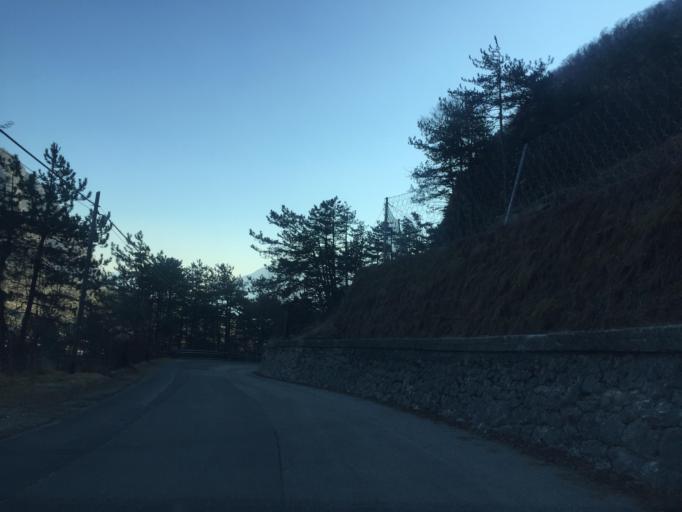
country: IT
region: Friuli Venezia Giulia
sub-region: Provincia di Udine
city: Tolmezzo
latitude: 46.4098
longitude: 13.0420
